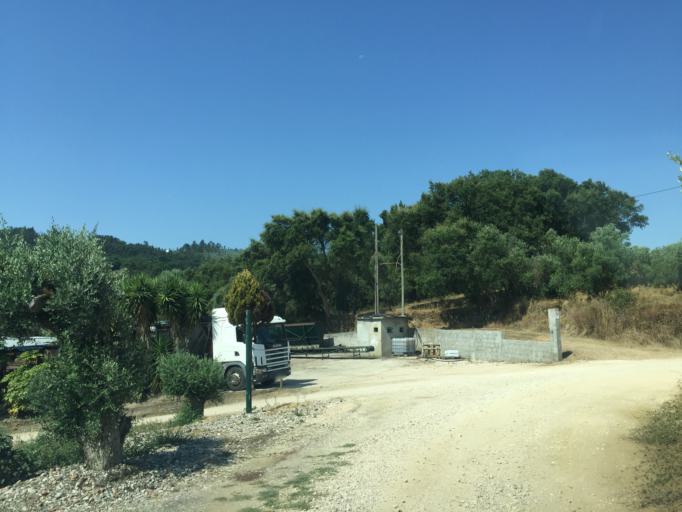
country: PT
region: Santarem
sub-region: Ferreira do Zezere
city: Ferreira do Zezere
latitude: 39.6061
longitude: -8.2829
